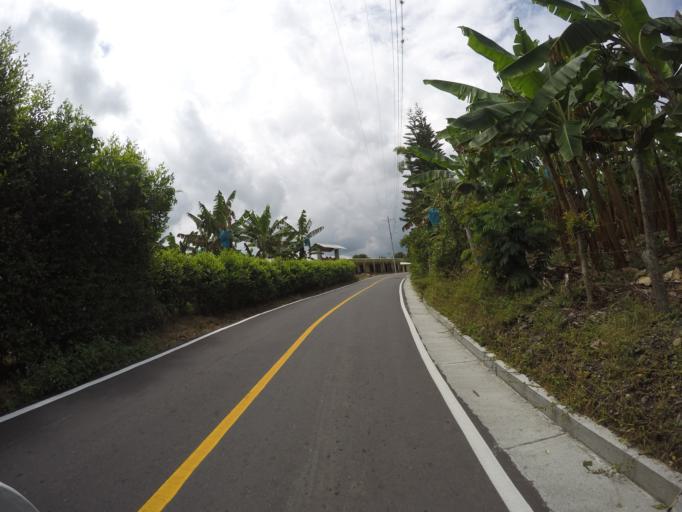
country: CO
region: Quindio
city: Quimbaya
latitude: 4.6128
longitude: -75.7560
